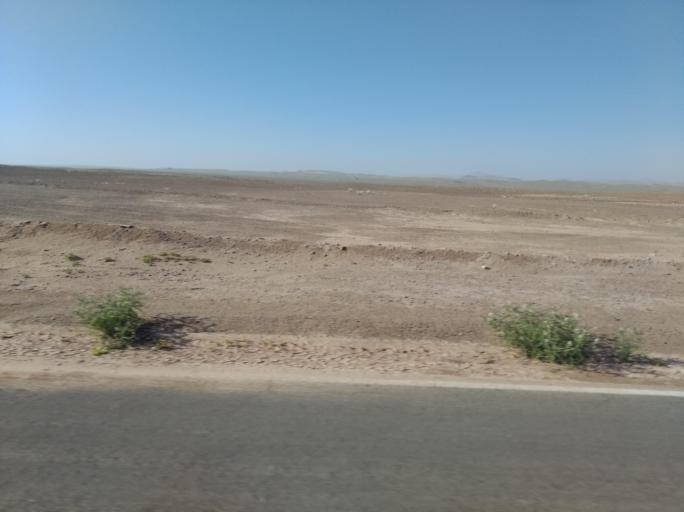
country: CL
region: Atacama
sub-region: Provincia de Copiapo
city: Copiapo
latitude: -27.3220
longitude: -70.8150
